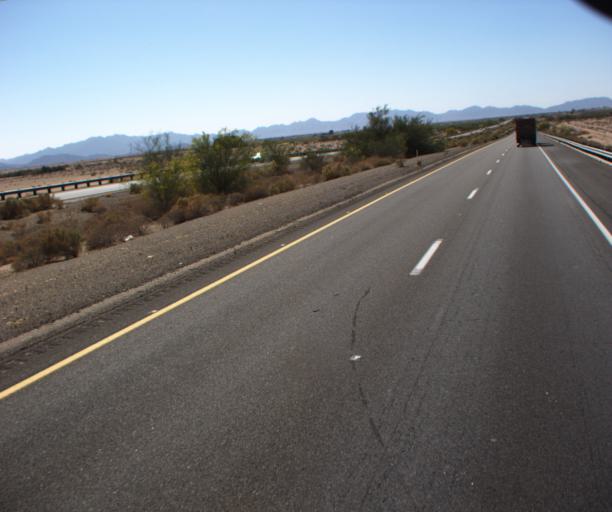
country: US
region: Arizona
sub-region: Yuma County
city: Wellton
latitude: 32.6765
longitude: -114.0499
